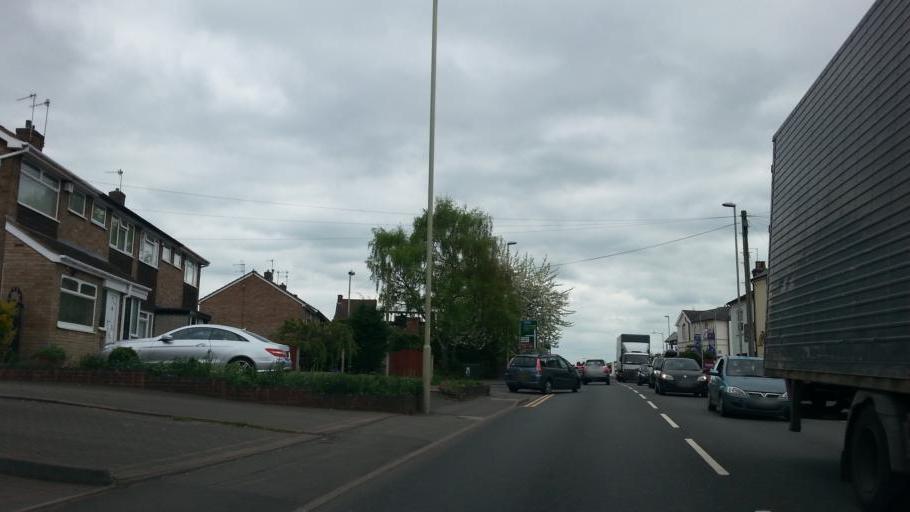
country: GB
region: England
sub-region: Dudley
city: Stourbridge
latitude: 52.4721
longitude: -2.1552
